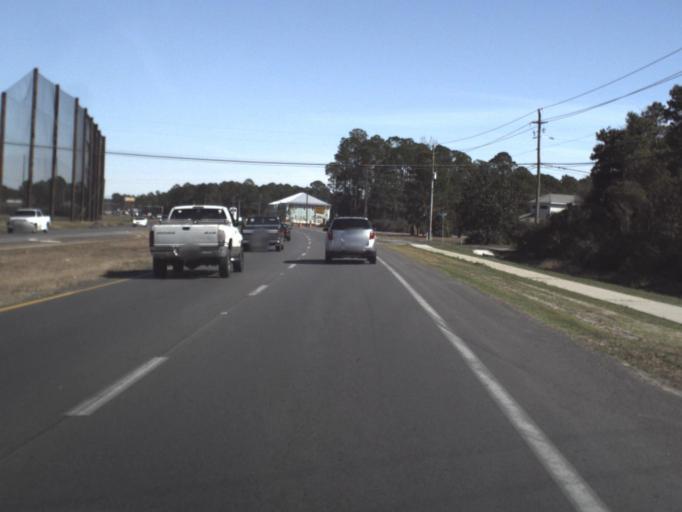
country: US
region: Florida
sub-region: Bay County
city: Panama City Beach
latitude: 30.2062
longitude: -85.8416
